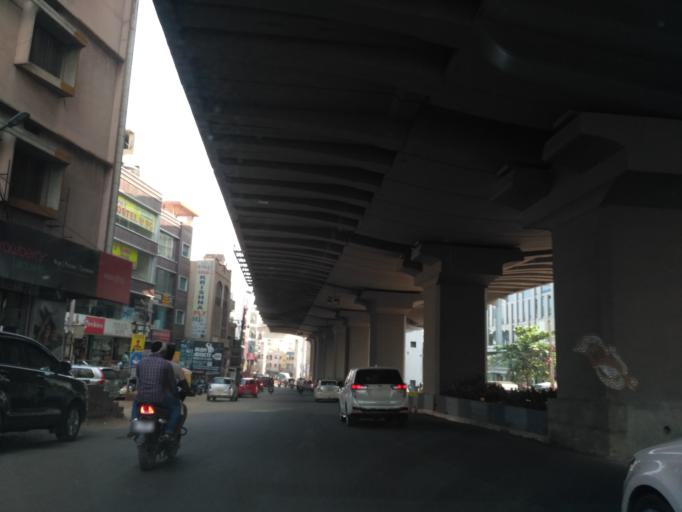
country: IN
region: Telangana
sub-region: Rangareddi
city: Kukatpalli
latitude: 17.4434
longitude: 78.3875
